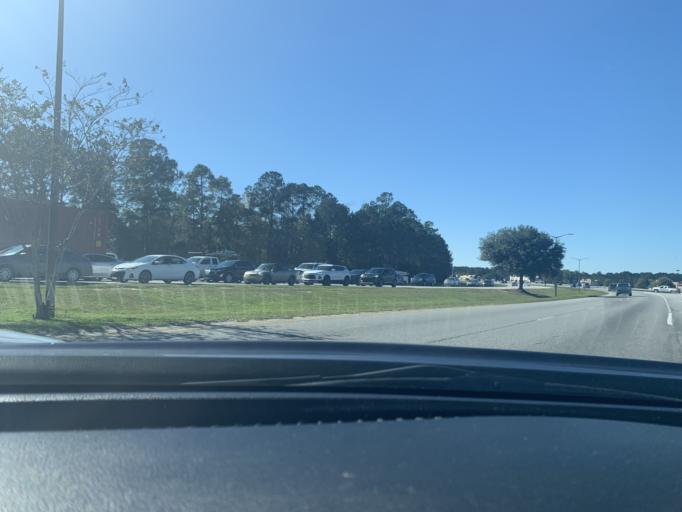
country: US
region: Georgia
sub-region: Chatham County
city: Pooler
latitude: 32.1408
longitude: -81.2474
